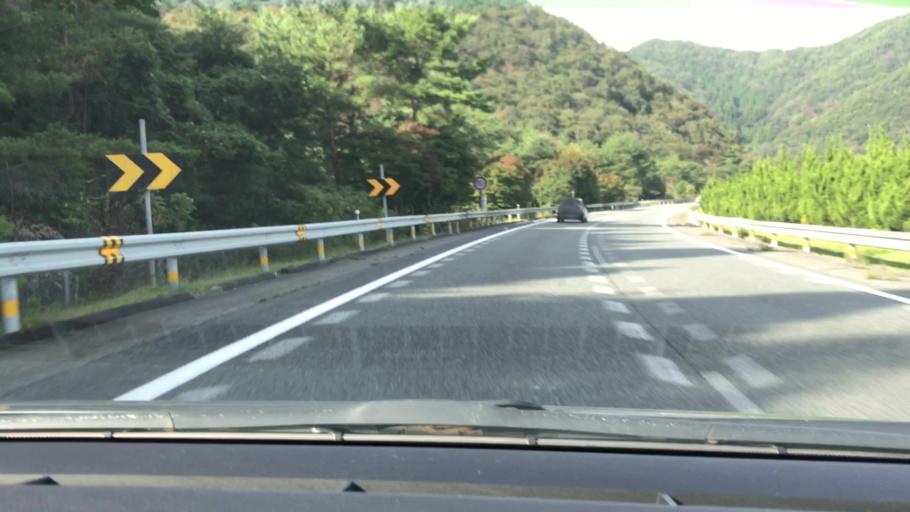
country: JP
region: Hyogo
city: Sasayama
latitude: 35.0150
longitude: 135.1701
